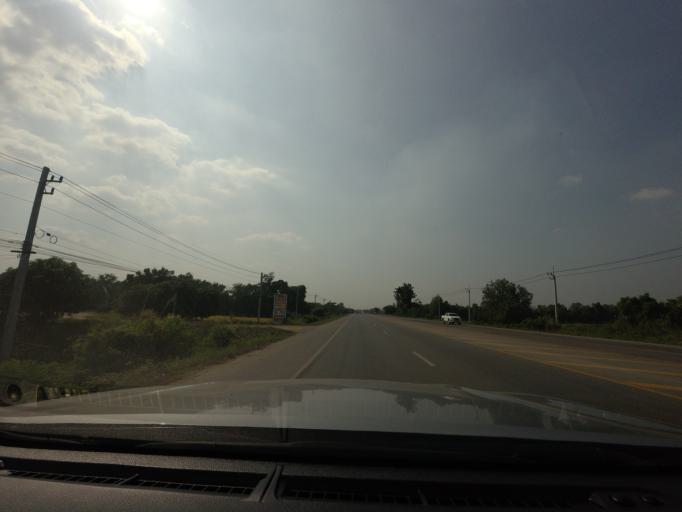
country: TH
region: Phitsanulok
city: Bang Rakam
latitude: 16.7654
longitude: 100.1349
